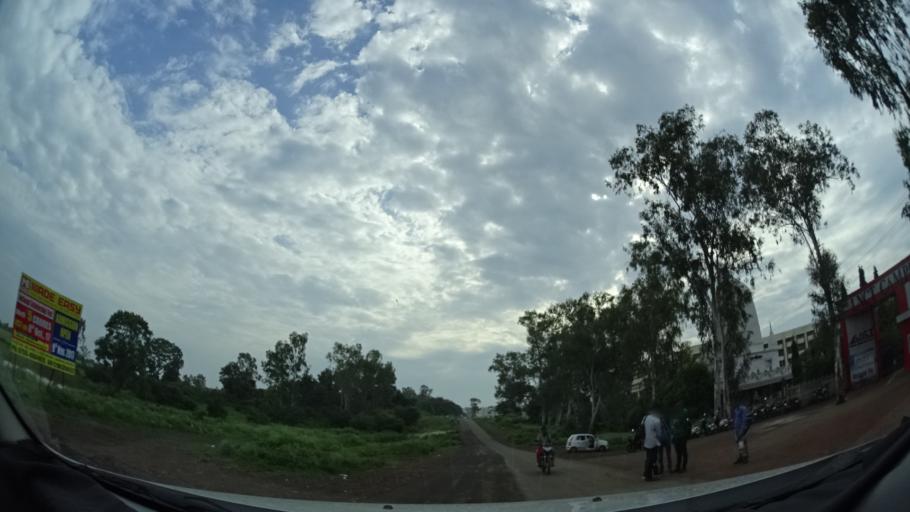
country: IN
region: Madhya Pradesh
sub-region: Bhopal
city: Bhopal
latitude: 23.2512
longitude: 77.5229
